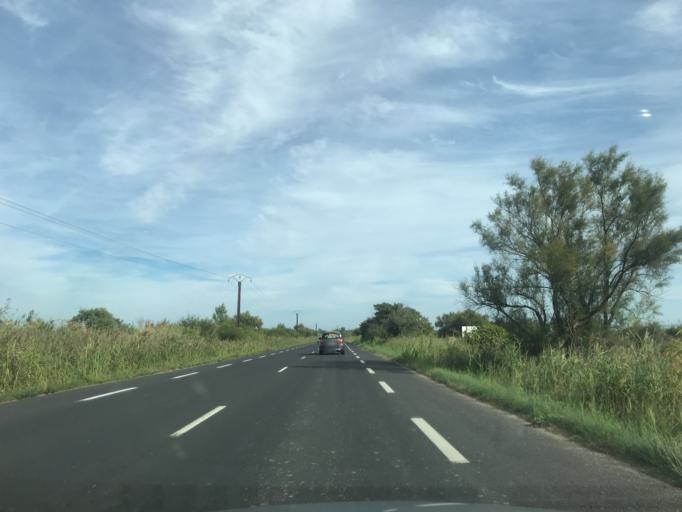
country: FR
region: Provence-Alpes-Cote d'Azur
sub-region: Departement des Bouches-du-Rhone
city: Saintes-Maries-de-la-Mer
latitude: 43.5528
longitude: 4.3308
